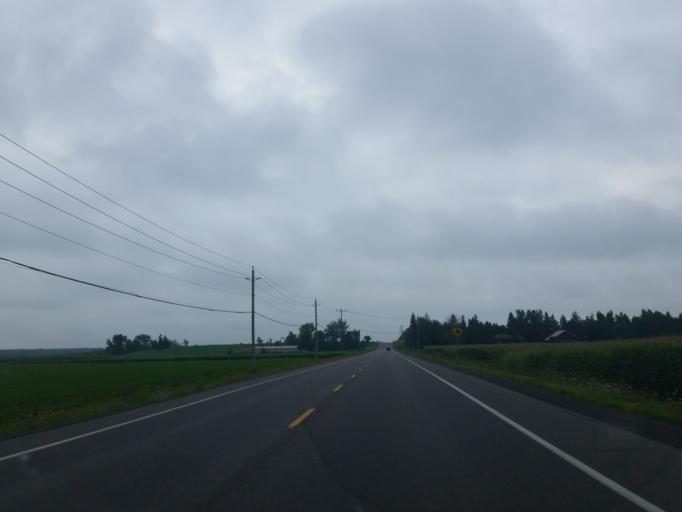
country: CA
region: Ontario
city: Clarence-Rockland
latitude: 45.4415
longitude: -75.4381
